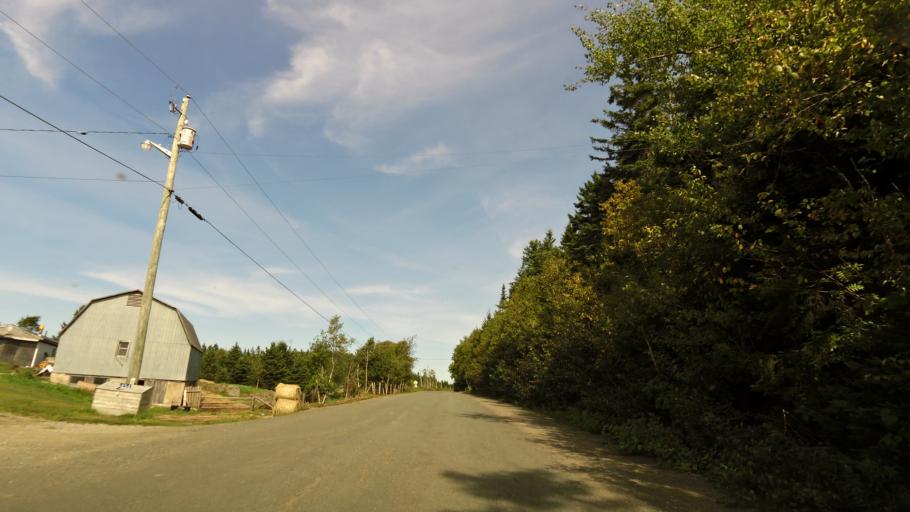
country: CA
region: New Brunswick
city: Hampton
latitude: 45.5641
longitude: -65.8429
